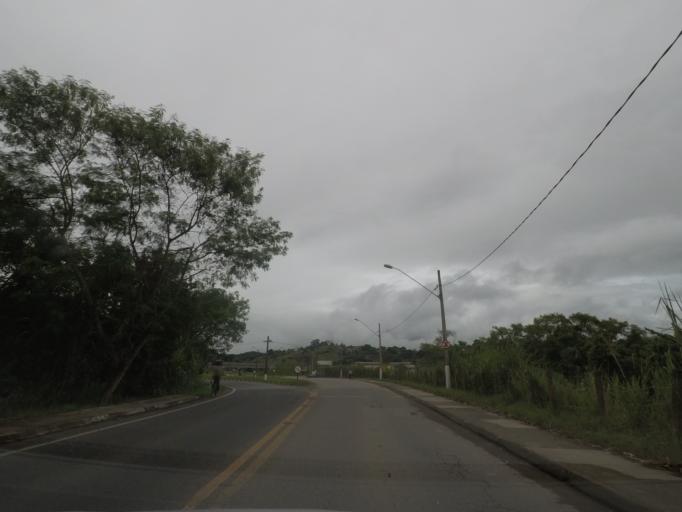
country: BR
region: Sao Paulo
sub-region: Cajati
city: Cajati
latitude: -24.7285
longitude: -48.0989
